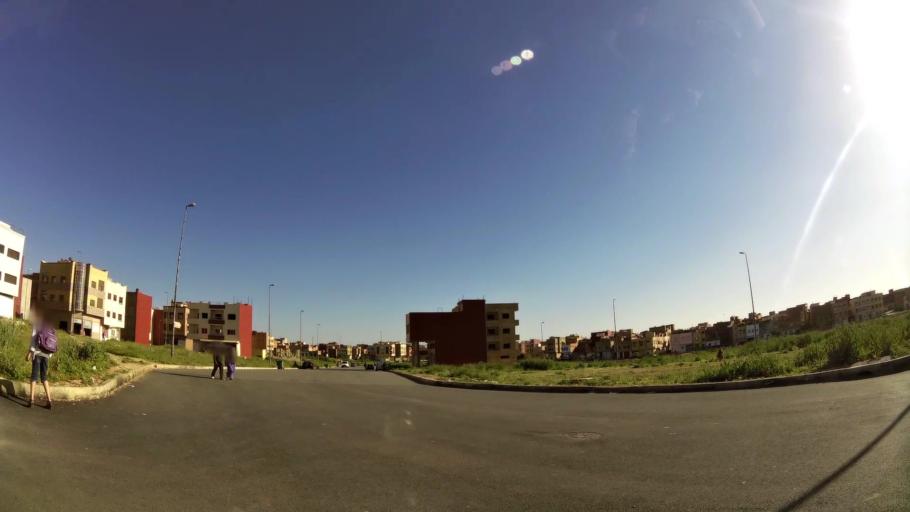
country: MA
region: Meknes-Tafilalet
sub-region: Meknes
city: Meknes
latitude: 33.8854
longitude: -5.5070
